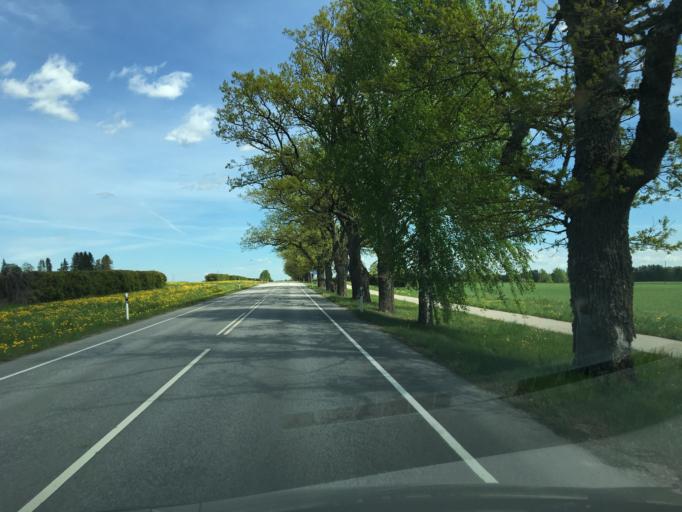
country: EE
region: Vorumaa
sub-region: Antsla vald
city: Vana-Antsla
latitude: 57.9162
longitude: 26.3074
